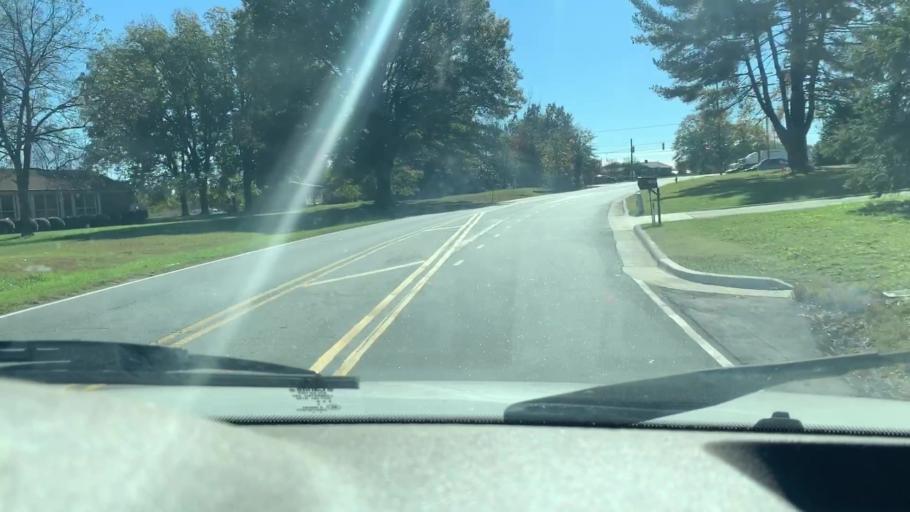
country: US
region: North Carolina
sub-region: Lincoln County
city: Lowesville
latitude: 35.4444
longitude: -80.9896
